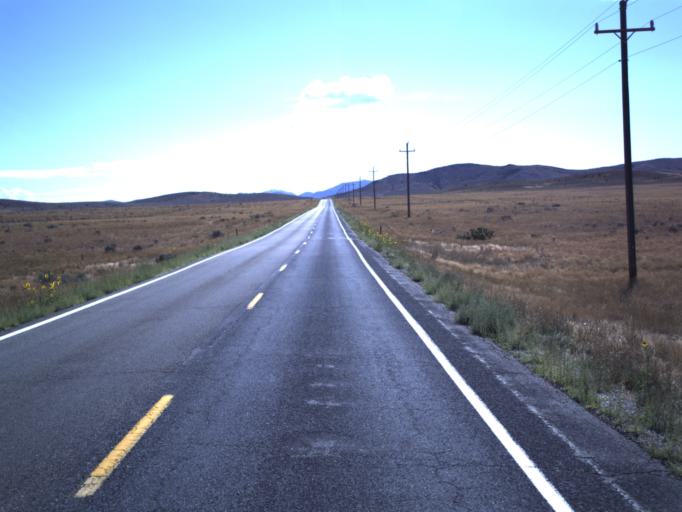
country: US
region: Utah
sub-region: Tooele County
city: Tooele
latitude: 40.0830
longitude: -112.4138
